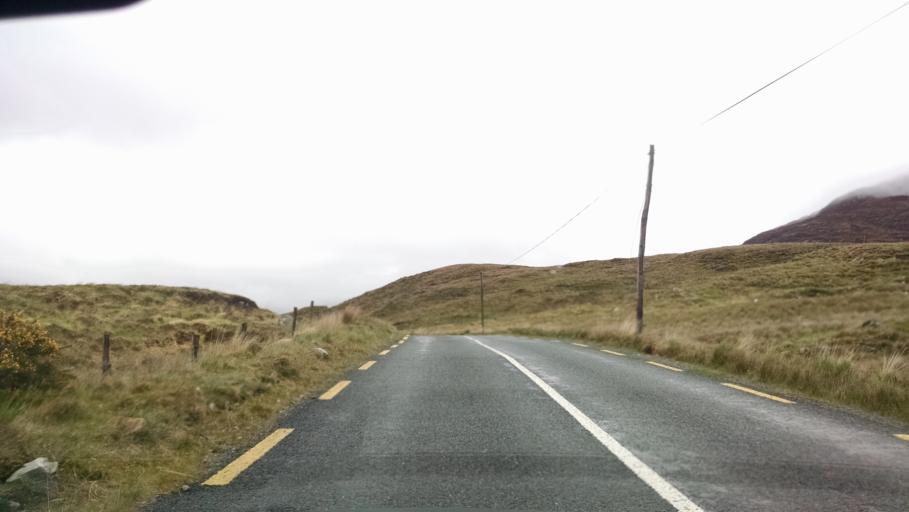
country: IE
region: Connaught
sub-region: County Galway
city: Clifden
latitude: 53.4777
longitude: -9.7423
